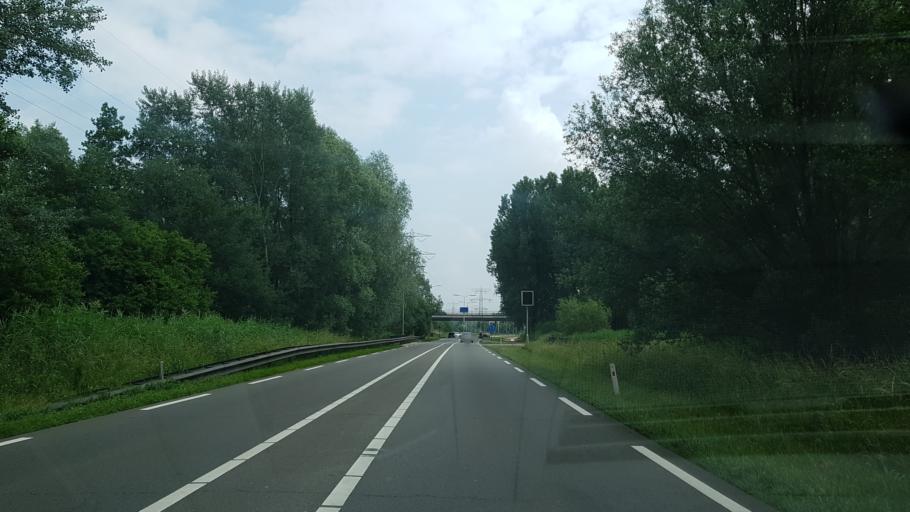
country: NL
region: North Brabant
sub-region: Gemeente Helmond
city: Helmond
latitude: 51.4992
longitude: 5.6772
